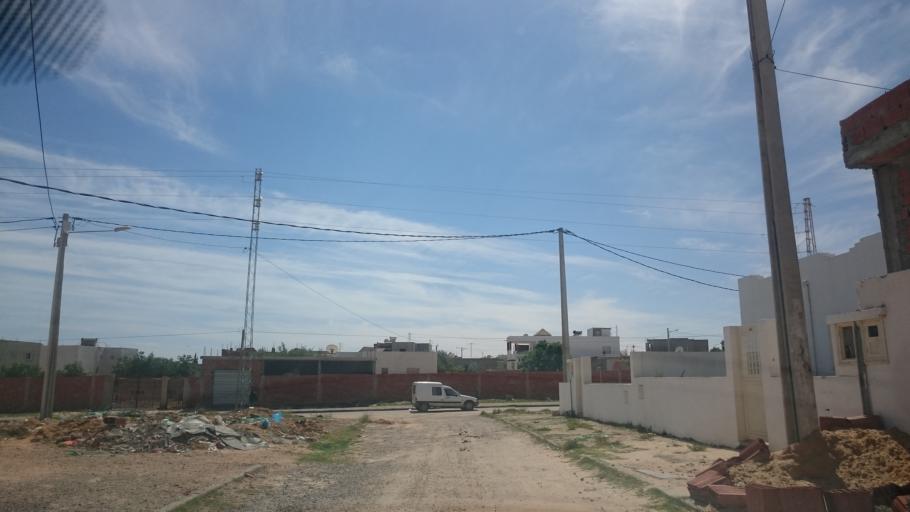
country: TN
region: Safaqis
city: Sfax
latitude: 34.7473
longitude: 10.5132
